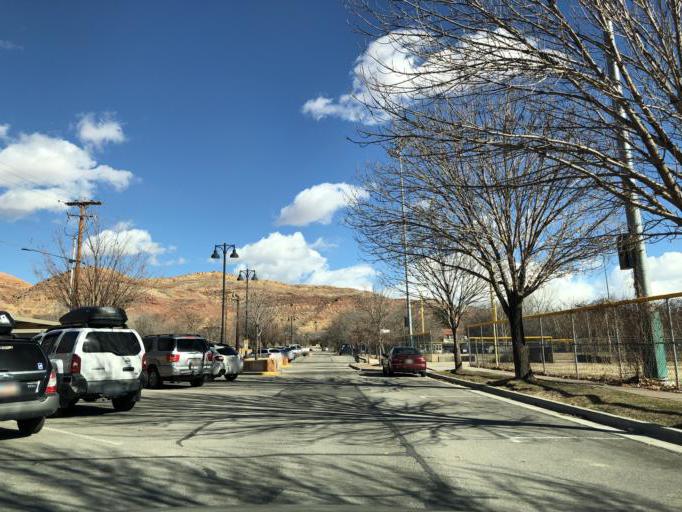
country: US
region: Utah
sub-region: Grand County
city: Moab
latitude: 38.5733
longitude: -109.5465
